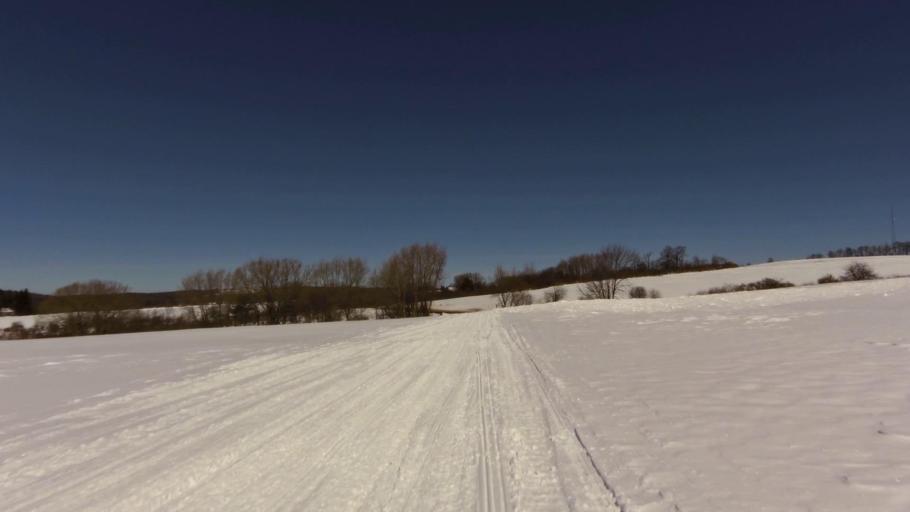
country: US
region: New York
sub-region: Allegany County
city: Houghton
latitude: 42.4294
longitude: -78.3090
